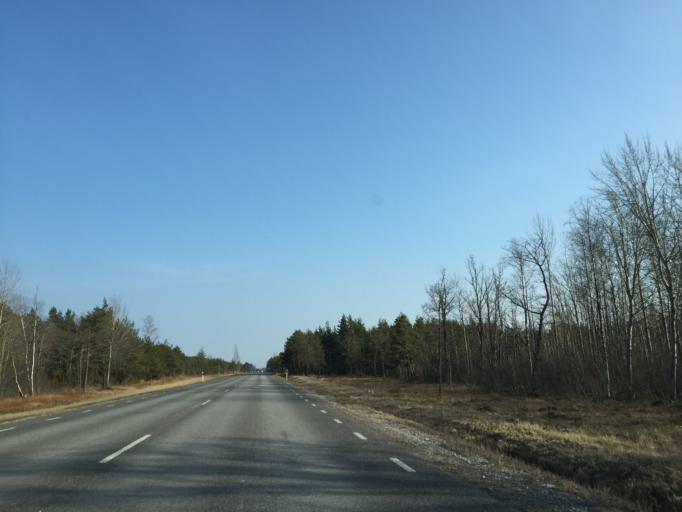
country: EE
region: Saare
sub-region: Orissaare vald
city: Orissaare
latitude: 58.5804
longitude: 23.3591
